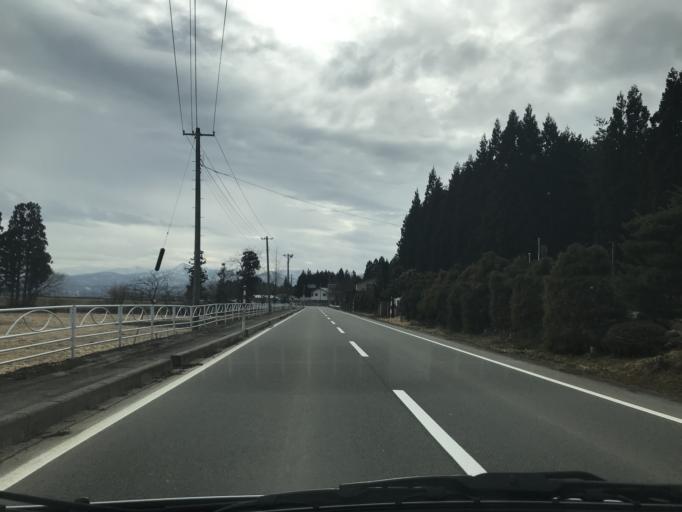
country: JP
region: Iwate
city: Hanamaki
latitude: 39.3517
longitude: 140.9850
